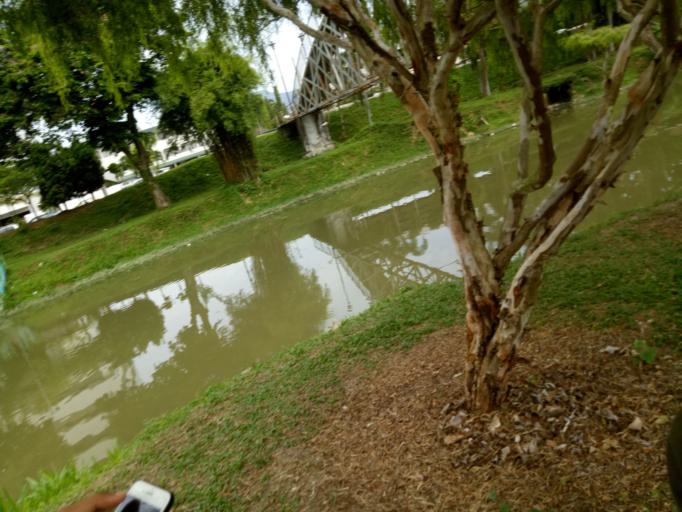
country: MY
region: Perak
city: Ipoh
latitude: 4.5999
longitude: 101.0790
